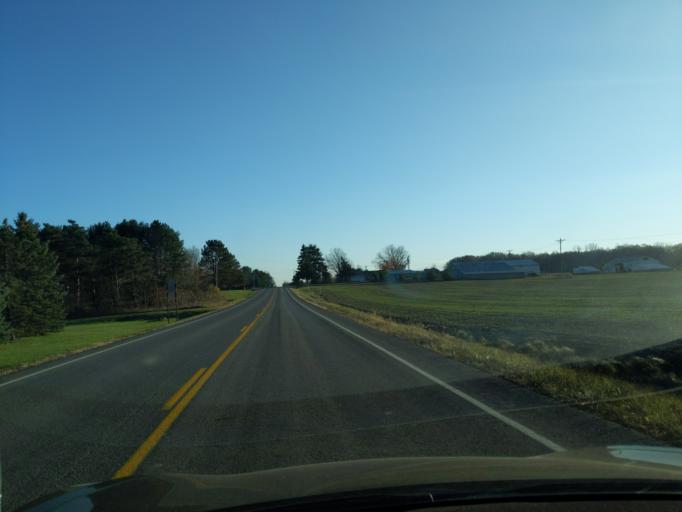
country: US
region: Michigan
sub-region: Ingham County
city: Williamston
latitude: 42.7289
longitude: -84.3163
